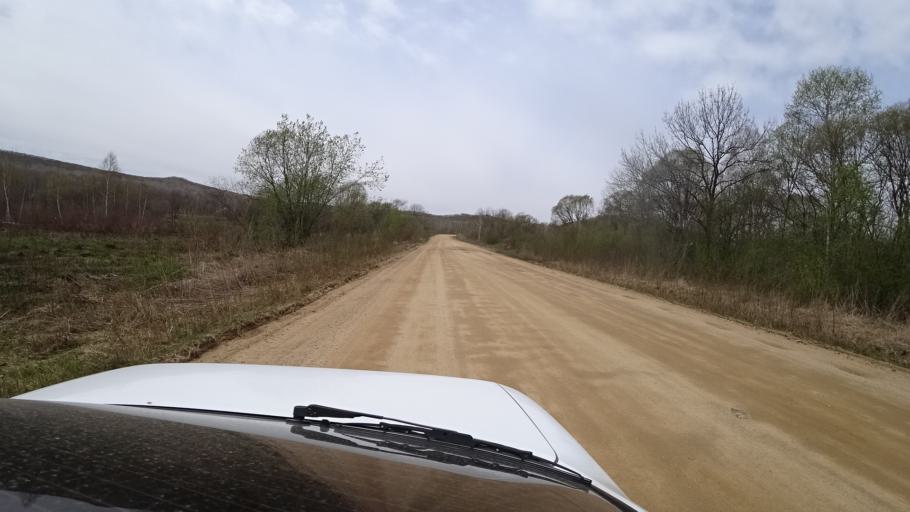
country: RU
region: Primorskiy
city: Dal'nerechensk
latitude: 45.7998
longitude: 134.0983
